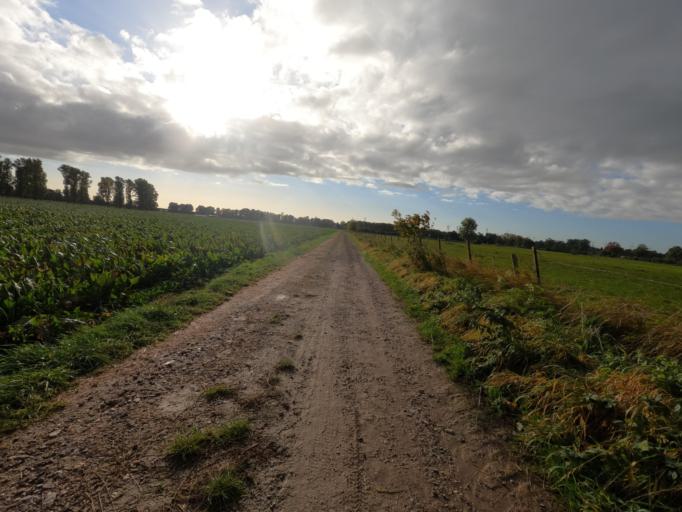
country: DE
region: North Rhine-Westphalia
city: Huckelhoven
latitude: 51.0201
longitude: 6.2347
